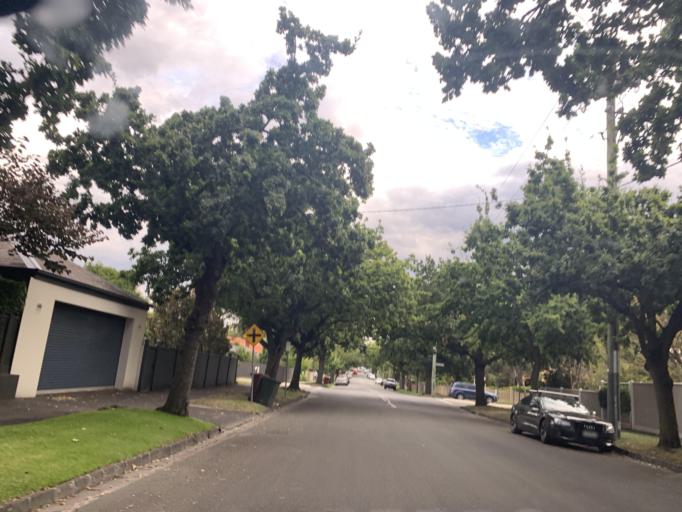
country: AU
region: Victoria
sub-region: Stonnington
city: Malvern East
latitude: -37.8707
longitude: 145.0434
